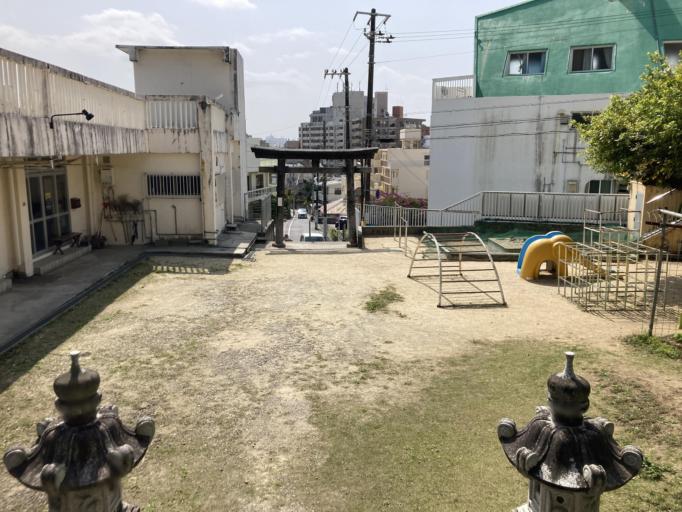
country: JP
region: Okinawa
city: Naha-shi
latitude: 26.2211
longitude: 127.6949
